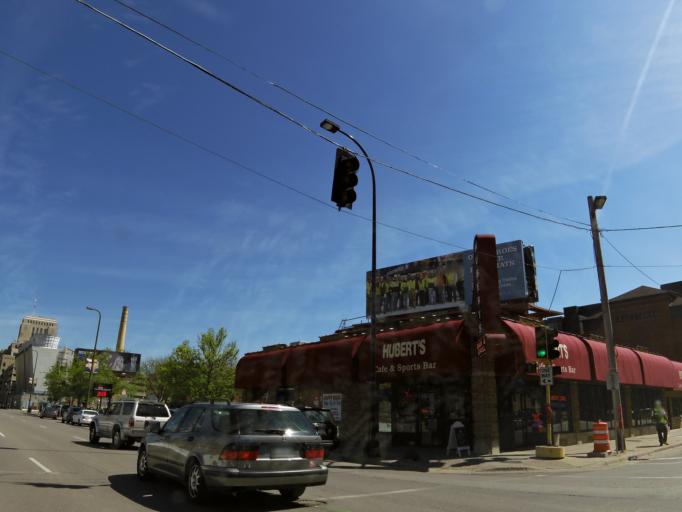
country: US
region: Minnesota
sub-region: Hennepin County
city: Minneapolis
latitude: 44.9733
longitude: -93.2605
